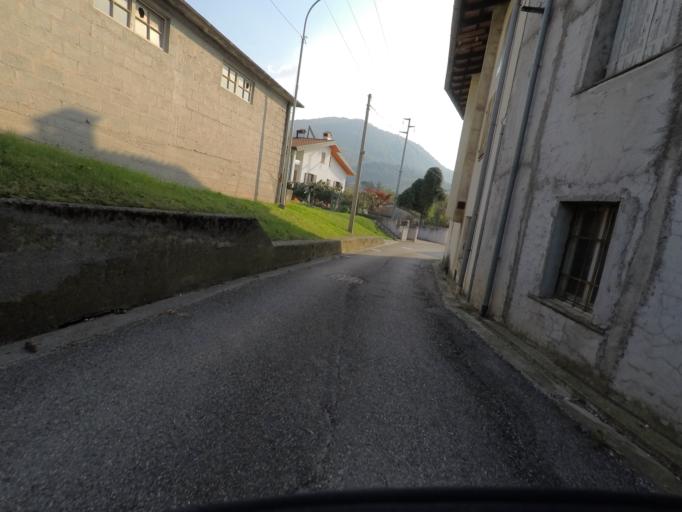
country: IT
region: Friuli Venezia Giulia
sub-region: Provincia di Udine
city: Artegna
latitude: 46.2454
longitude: 13.1478
